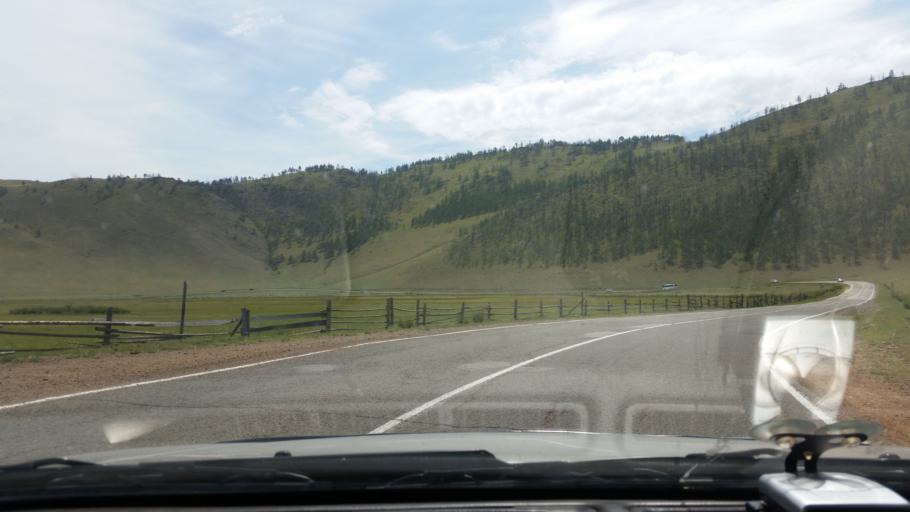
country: RU
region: Irkutsk
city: Yelantsy
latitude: 52.8051
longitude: 106.4703
